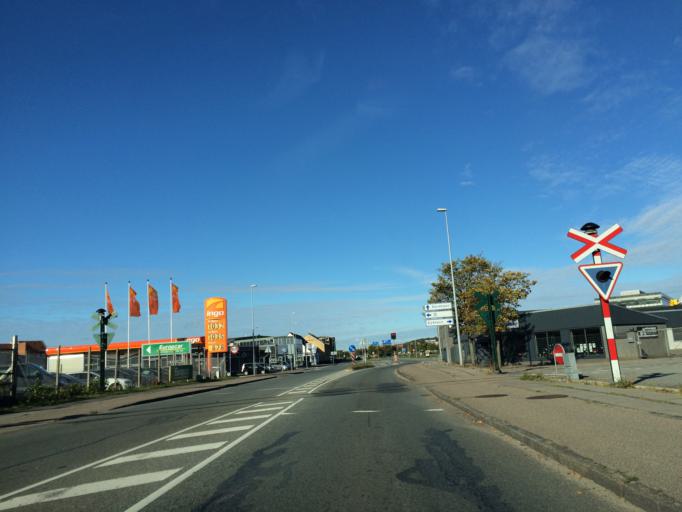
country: DK
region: Central Jutland
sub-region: Randers Kommune
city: Randers
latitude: 56.4534
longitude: 10.0471
